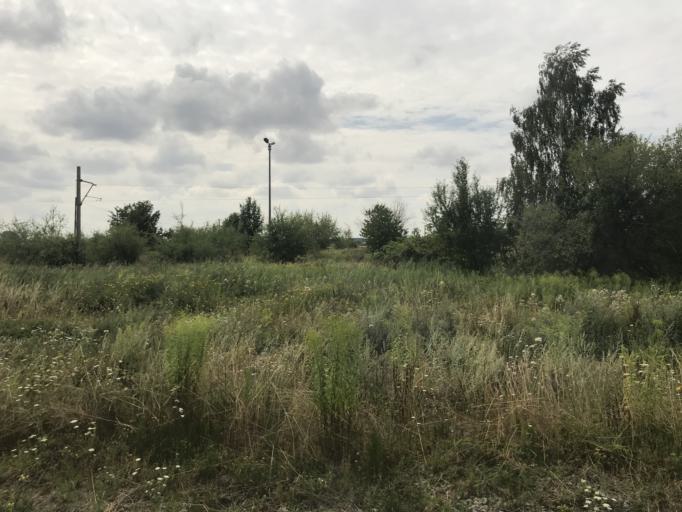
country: PL
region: Greater Poland Voivodeship
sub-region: Powiat gnieznienski
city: Gniezno
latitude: 52.5323
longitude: 17.6403
